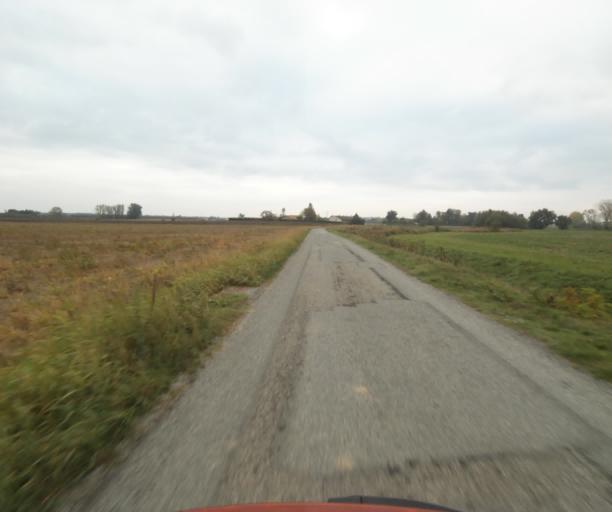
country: FR
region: Midi-Pyrenees
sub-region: Departement du Tarn-et-Garonne
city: Verdun-sur-Garonne
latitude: 43.8139
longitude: 1.2216
